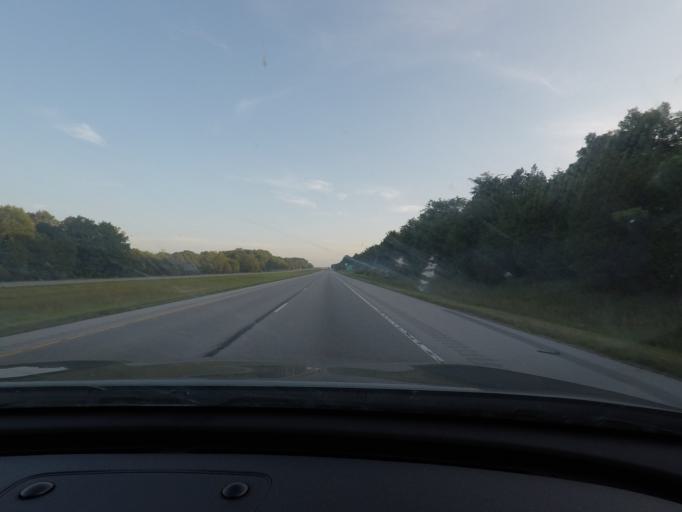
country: US
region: Illinois
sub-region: Johnson County
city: Goreville
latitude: 37.5220
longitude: -88.9147
